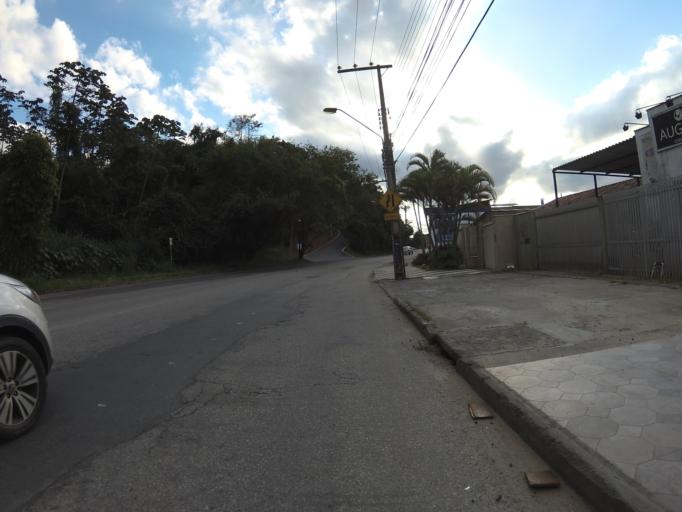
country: BR
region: Santa Catarina
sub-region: Blumenau
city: Blumenau
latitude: -26.8830
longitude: -49.1062
